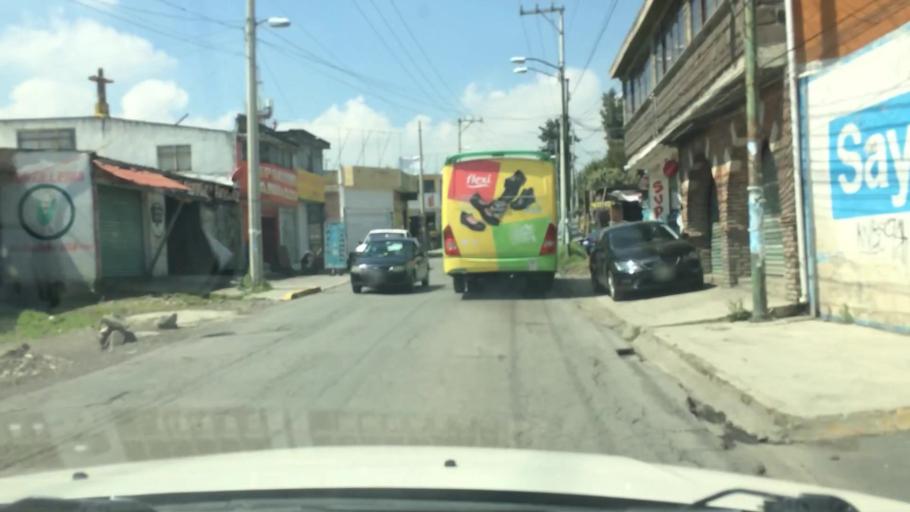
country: MX
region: Mexico City
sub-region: Tlalpan
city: Lomas de Tepemecatl
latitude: 19.2339
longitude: -99.1912
